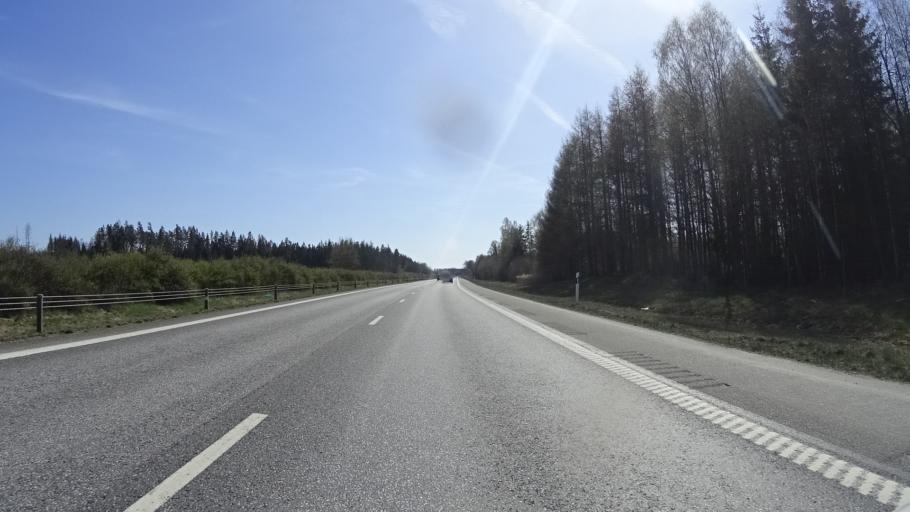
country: SE
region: Joenkoeping
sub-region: Varnamo Kommun
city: Varnamo
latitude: 57.1508
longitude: 14.0699
